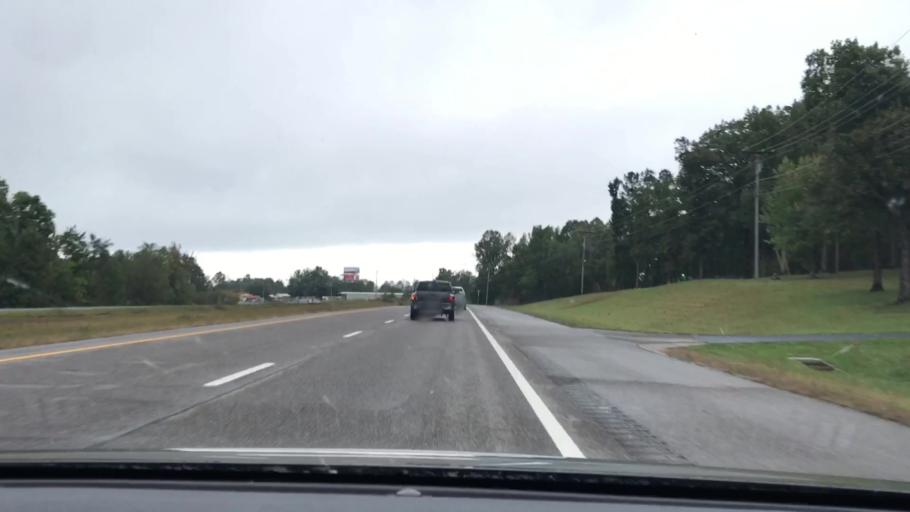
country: US
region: Tennessee
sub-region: Fentress County
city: Jamestown
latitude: 36.3849
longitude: -84.9391
